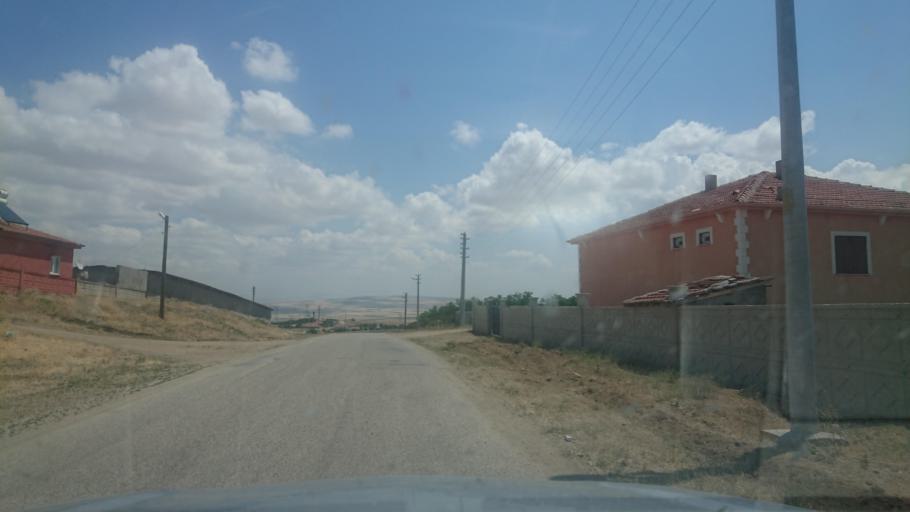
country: TR
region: Aksaray
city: Agacoren
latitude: 38.8753
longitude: 33.9440
